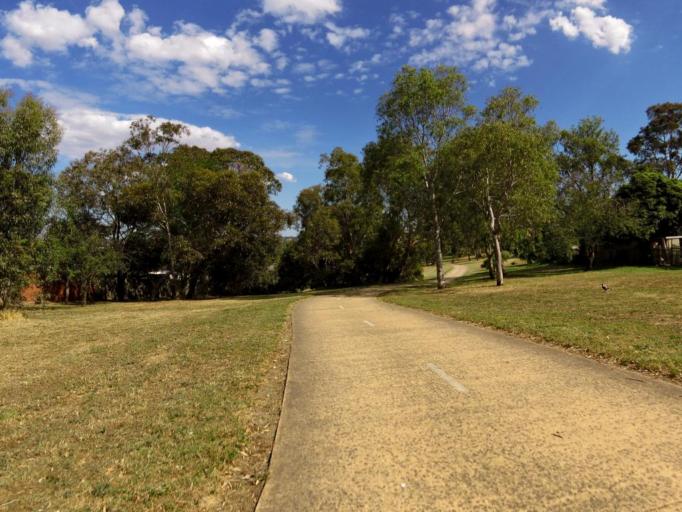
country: AU
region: Victoria
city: Rosanna
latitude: -37.7461
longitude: 145.0801
